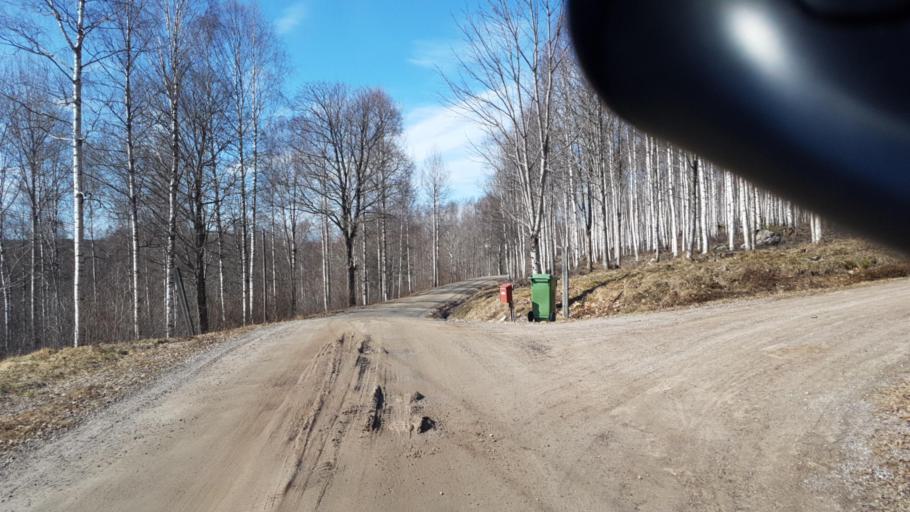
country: SE
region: Vaermland
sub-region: Arvika Kommun
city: Arvika
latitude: 59.7139
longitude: 12.8478
